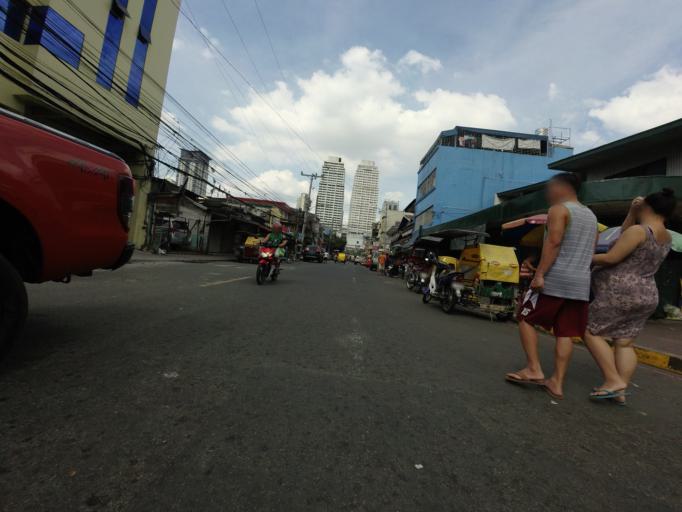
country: PH
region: Metro Manila
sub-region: City of Manila
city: Port Area
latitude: 14.5680
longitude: 120.9894
